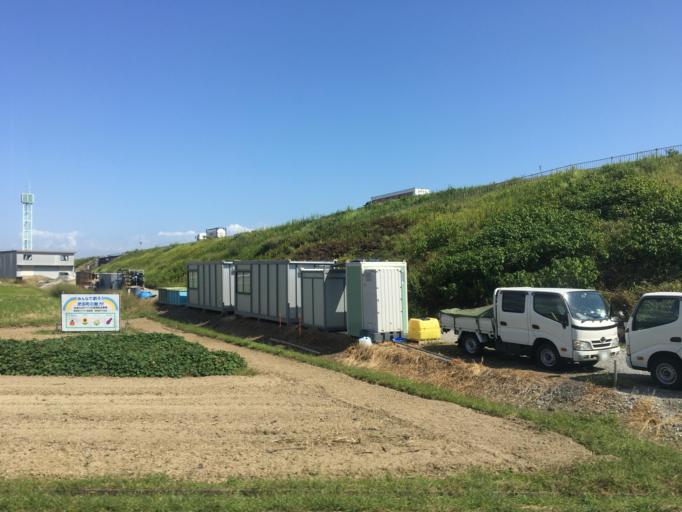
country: JP
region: Mie
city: Suzuka
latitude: 34.8747
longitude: 136.5935
